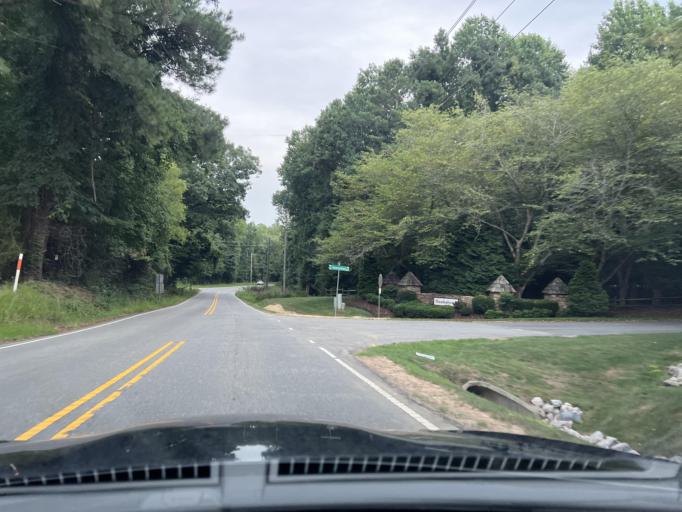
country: US
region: North Carolina
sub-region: Wake County
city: Wake Forest
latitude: 36.0082
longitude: -78.5330
